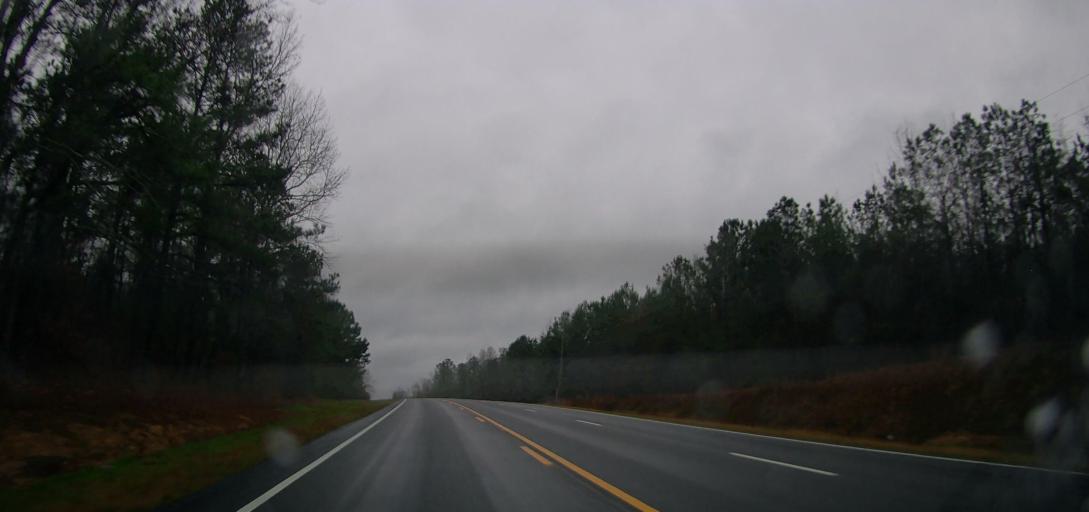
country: US
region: Alabama
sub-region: Bibb County
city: Centreville
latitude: 32.8194
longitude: -86.9403
